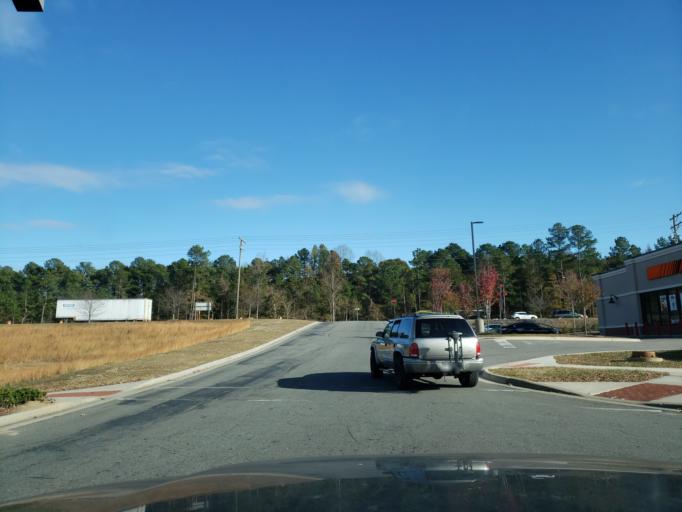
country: US
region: North Carolina
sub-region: Durham County
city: Durham
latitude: 35.9413
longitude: -78.9074
